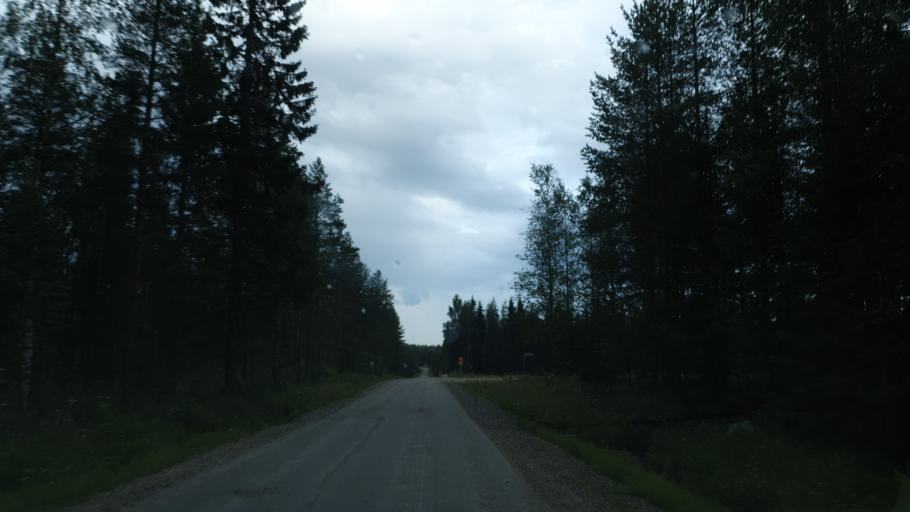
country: FI
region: Kainuu
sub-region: Kehys-Kainuu
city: Kuhmo
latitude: 64.2123
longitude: 29.3692
